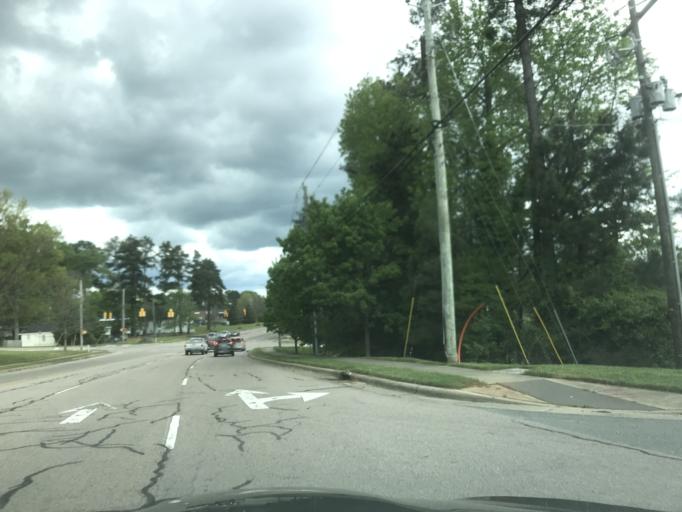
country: US
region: North Carolina
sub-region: Wake County
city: West Raleigh
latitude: 35.7829
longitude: -78.7216
